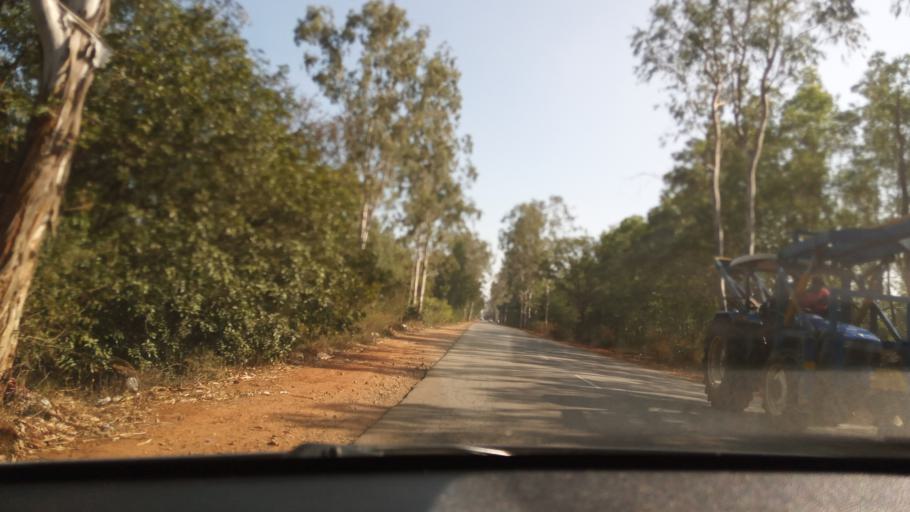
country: IN
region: Karnataka
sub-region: Bangalore Rural
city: Devanhalli
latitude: 13.2681
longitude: 77.7435
